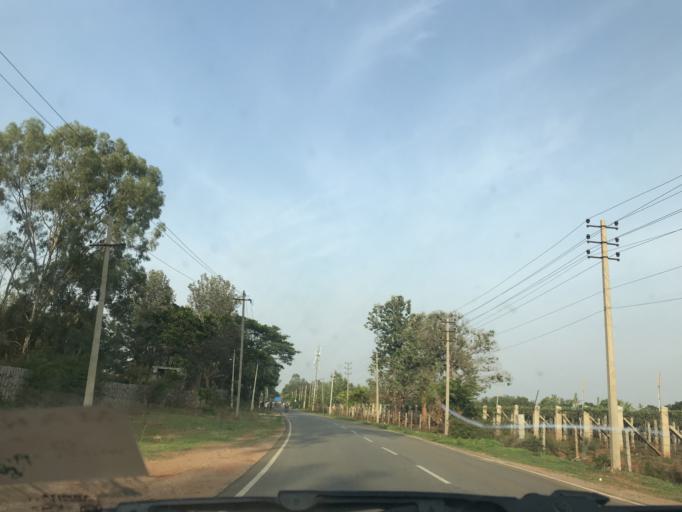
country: IN
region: Karnataka
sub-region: Bangalore Rural
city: Devanhalli
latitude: 13.2294
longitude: 77.6714
